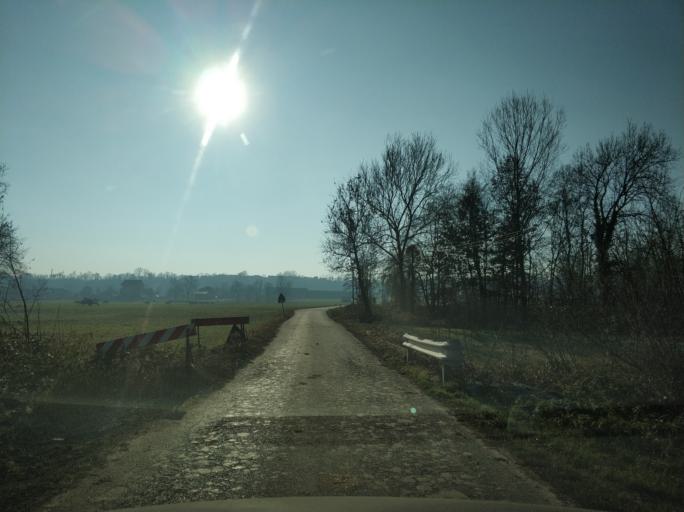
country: IT
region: Piedmont
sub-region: Provincia di Torino
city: Levone
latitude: 45.3026
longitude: 7.6151
